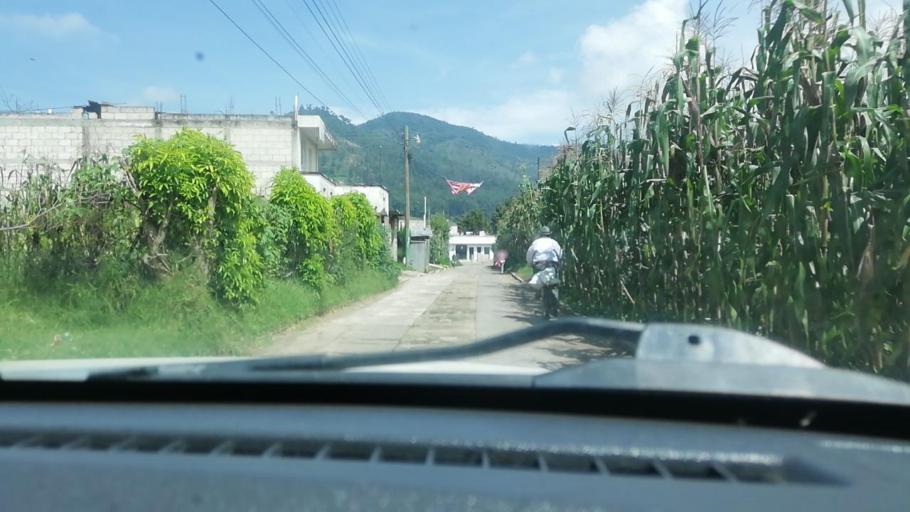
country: GT
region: Totonicapan
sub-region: Municipio de San Andres Xecul
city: San Andres Xecul
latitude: 14.8890
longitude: -91.4726
